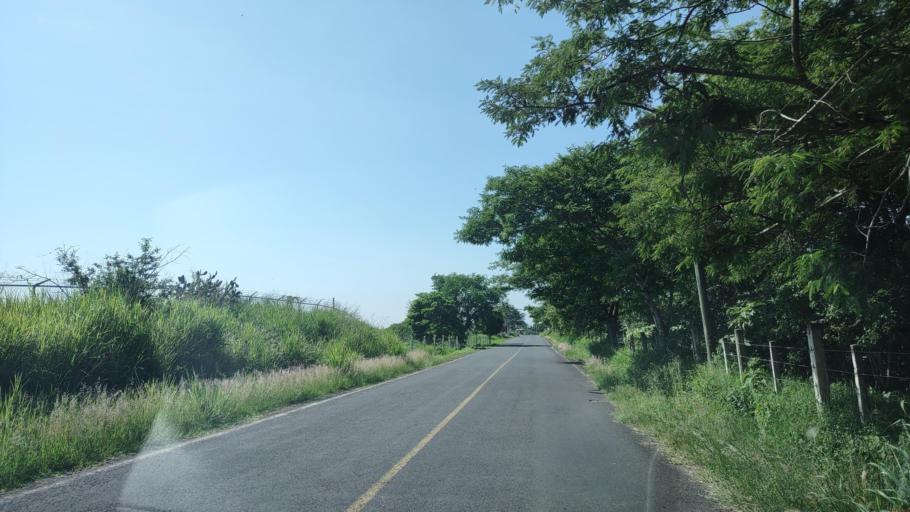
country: MX
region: Veracruz
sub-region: Emiliano Zapata
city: Dos Rios
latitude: 19.4932
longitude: -96.8231
